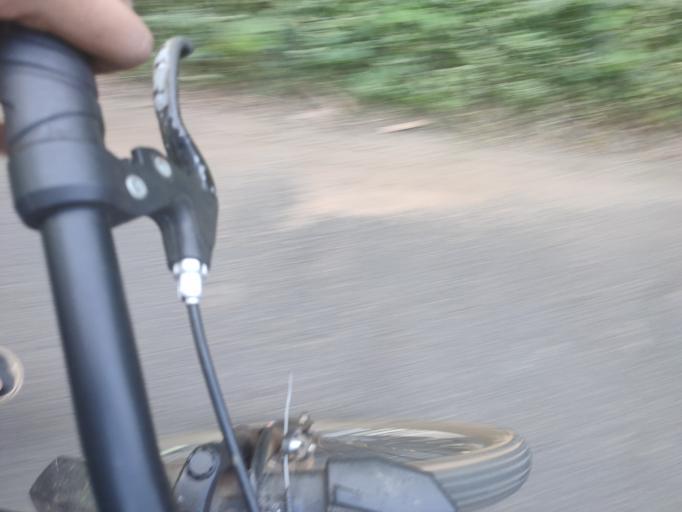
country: IN
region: Kerala
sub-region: Thrissur District
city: Kizhake Chalakudi
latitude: 10.2307
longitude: 76.3294
